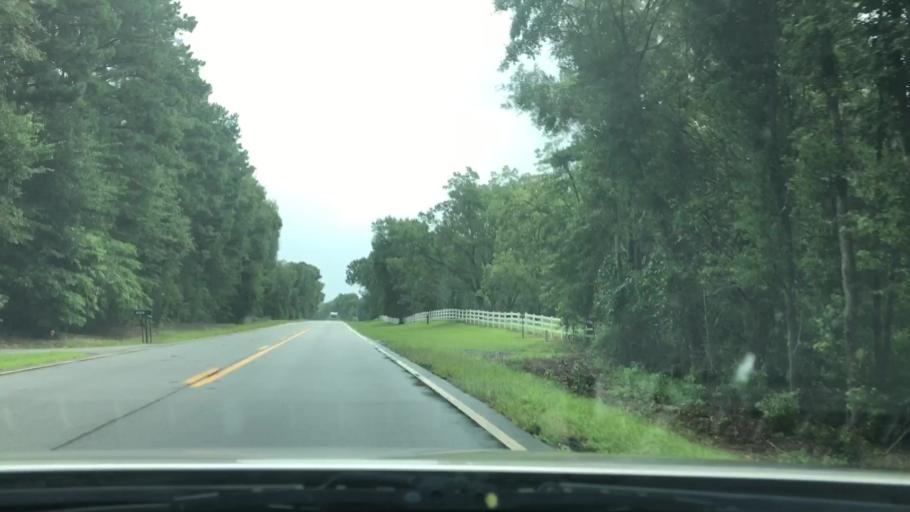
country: US
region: Georgia
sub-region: Pike County
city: Zebulon
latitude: 33.0885
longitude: -84.2733
